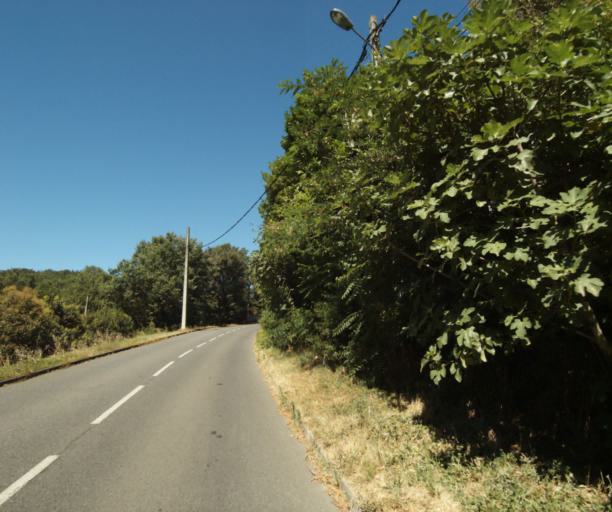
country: FR
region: Midi-Pyrenees
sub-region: Departement de la Haute-Garonne
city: Auzeville-Tolosane
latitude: 43.5140
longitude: 1.4819
